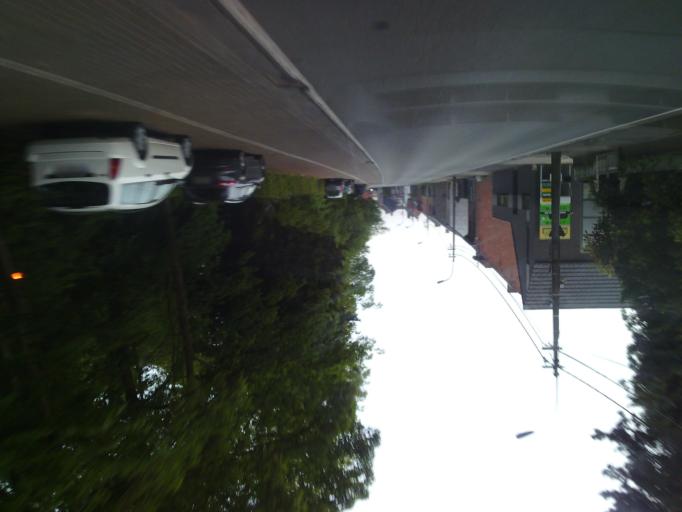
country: BE
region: Flanders
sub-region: Provincie Oost-Vlaanderen
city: Wichelen
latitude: 51.0456
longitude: 3.9469
